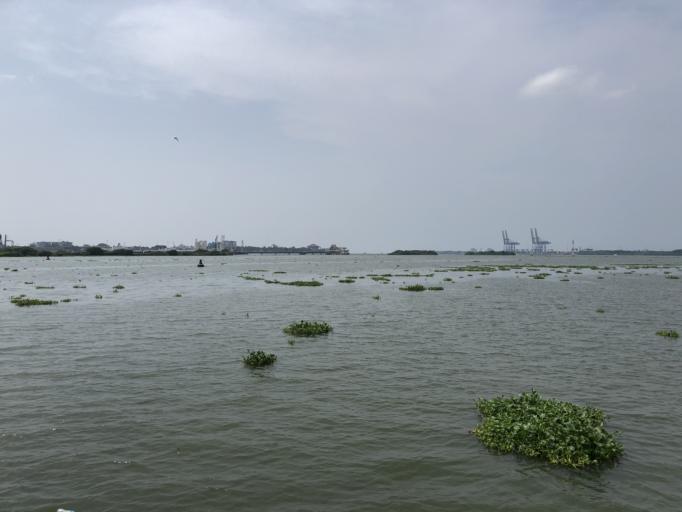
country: IN
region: Kerala
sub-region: Ernakulam
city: Cochin
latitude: 9.9747
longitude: 76.2767
